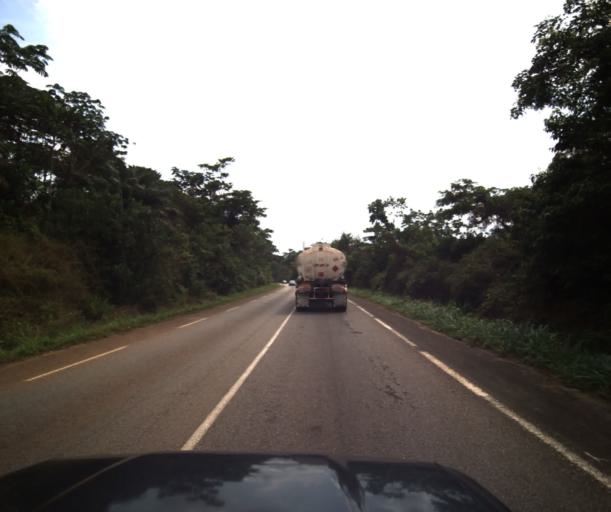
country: CM
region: Centre
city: Eseka
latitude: 3.8636
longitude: 10.5988
